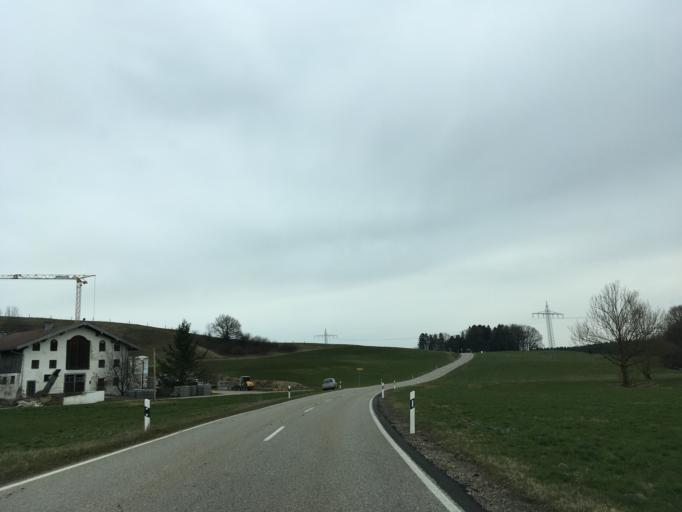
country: DE
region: Bavaria
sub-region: Upper Bavaria
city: Schnaitsee
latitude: 48.0649
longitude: 12.3809
